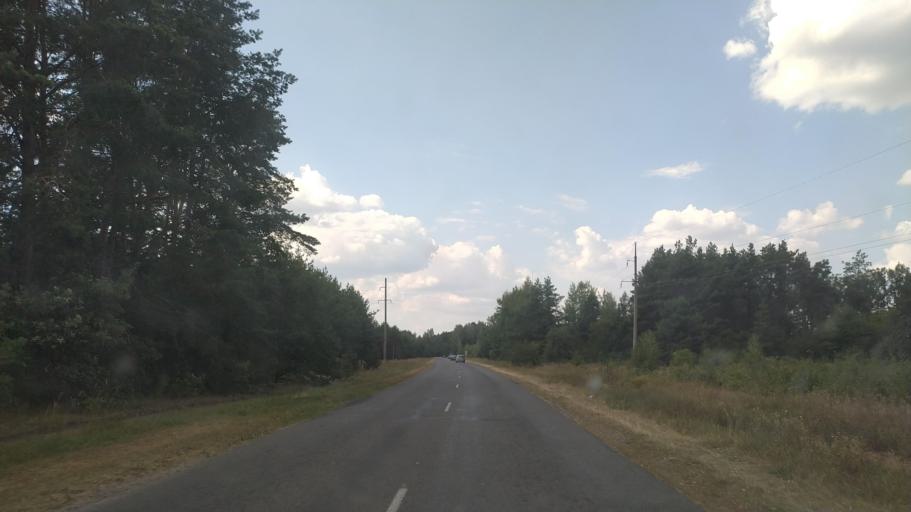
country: BY
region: Brest
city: Drahichyn
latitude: 52.1051
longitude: 25.1215
